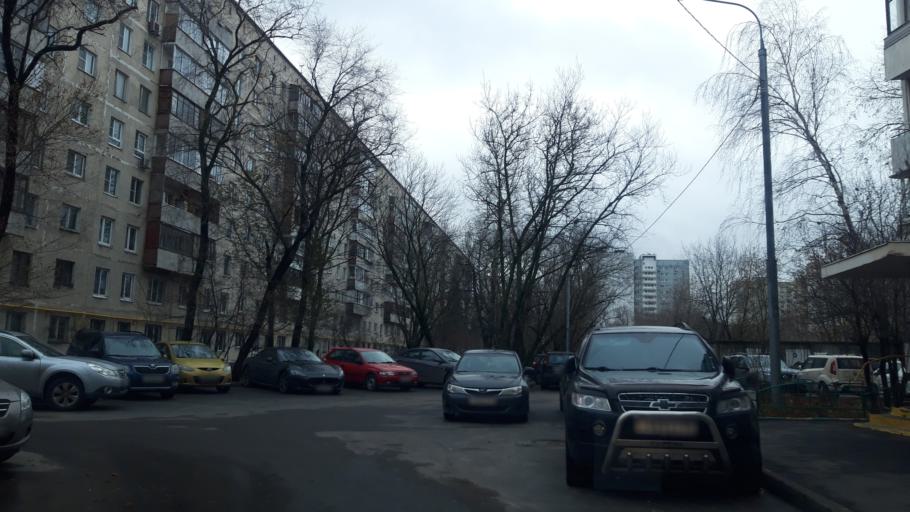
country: RU
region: Moscow
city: Likhobory
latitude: 55.8324
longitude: 37.5689
